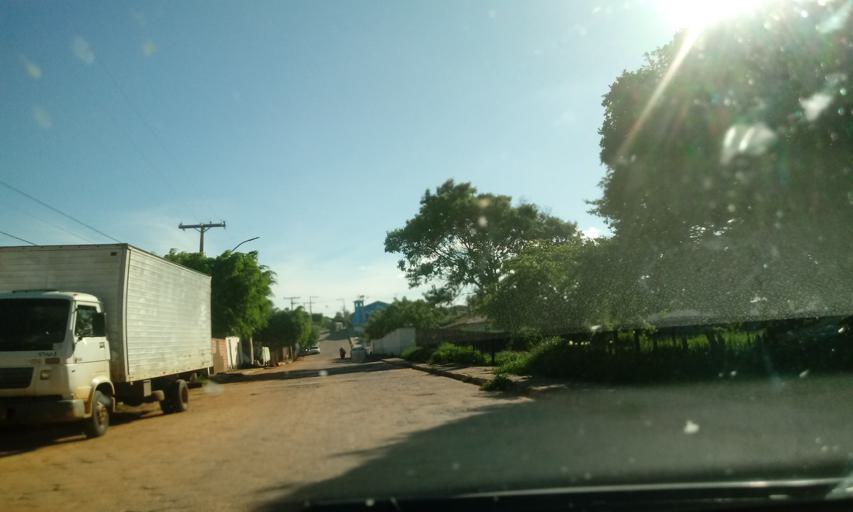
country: BR
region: Bahia
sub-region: Riacho De Santana
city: Riacho de Santana
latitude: -13.7755
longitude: -42.7189
